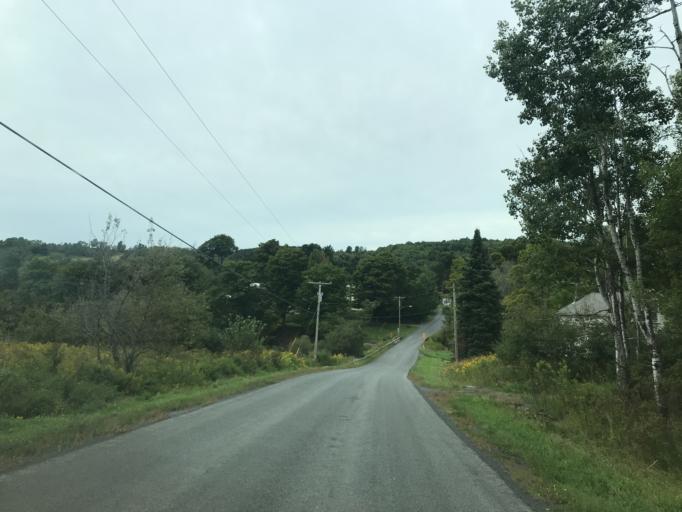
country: US
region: New York
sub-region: Otsego County
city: Worcester
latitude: 42.5429
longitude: -74.6631
